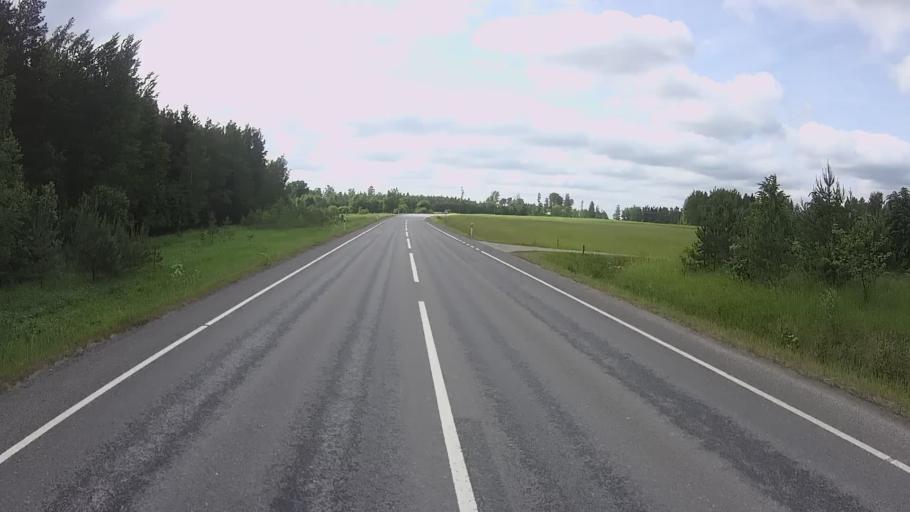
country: EE
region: Vorumaa
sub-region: Voru linn
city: Voru
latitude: 57.9249
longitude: 27.0345
